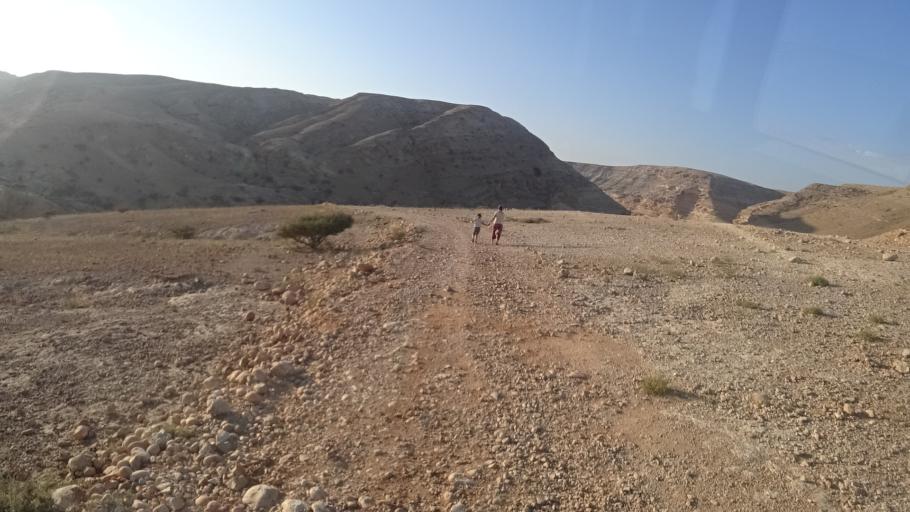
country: OM
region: Zufar
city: Salalah
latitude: 17.2442
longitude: 53.8906
